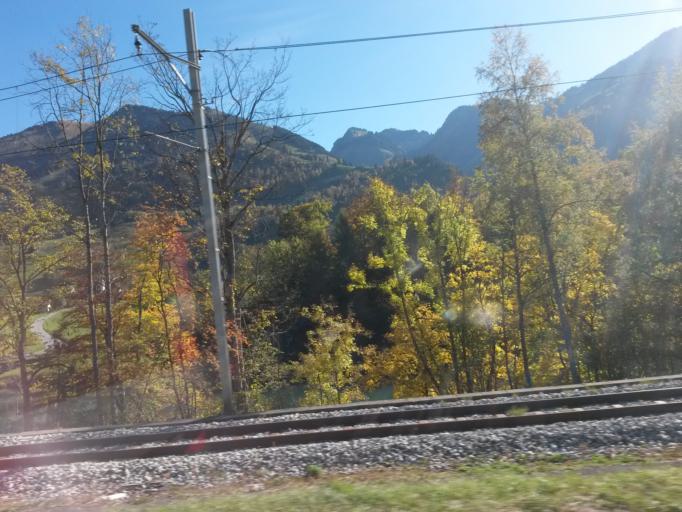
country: CH
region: Fribourg
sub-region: Gruyere District
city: Gruyeres
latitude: 46.5055
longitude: 7.0517
